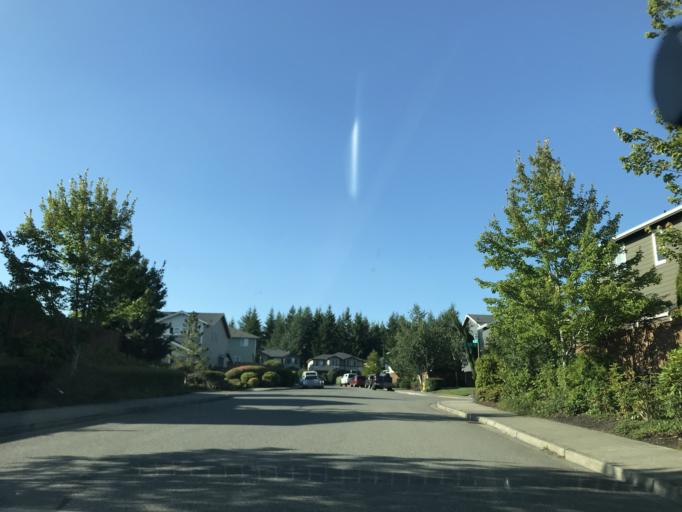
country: US
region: Washington
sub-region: King County
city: Ravensdale
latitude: 47.3546
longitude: -122.0003
